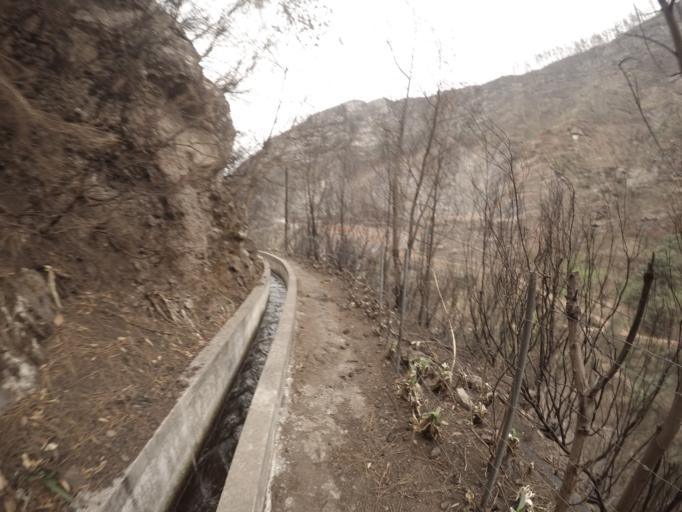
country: PT
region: Madeira
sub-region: Funchal
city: Nossa Senhora do Monte
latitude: 32.6907
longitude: -16.9161
